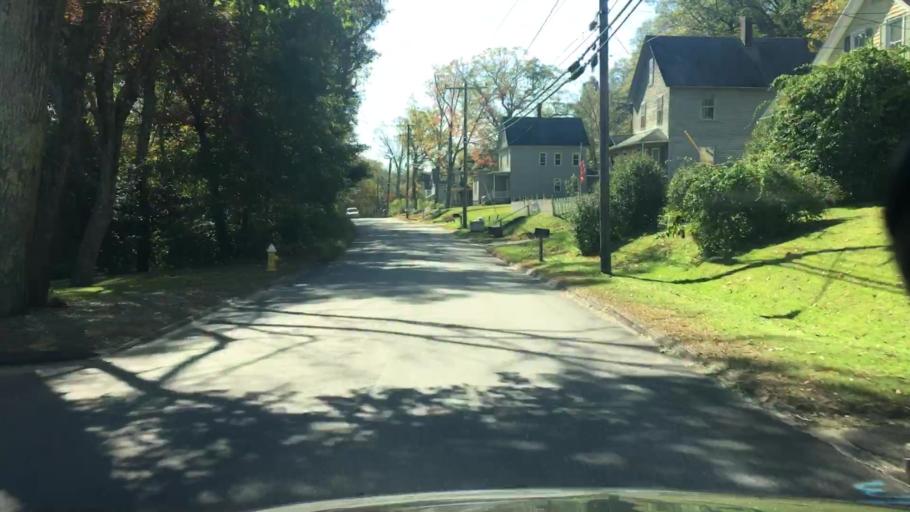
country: US
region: Connecticut
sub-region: Tolland County
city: Stafford Springs
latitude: 41.9625
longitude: -72.3005
